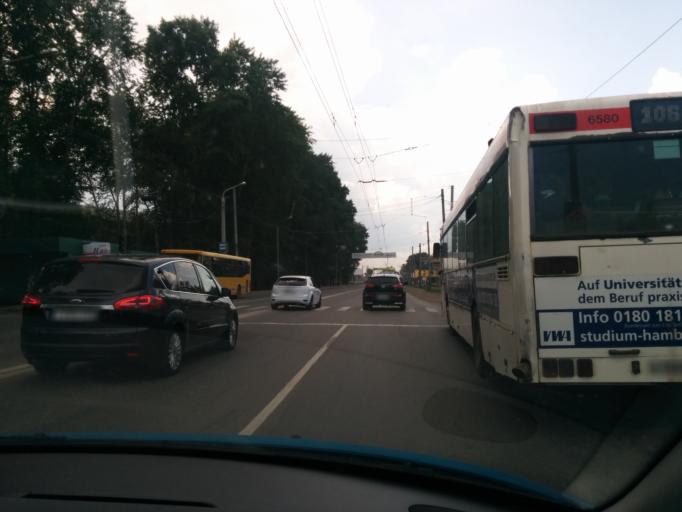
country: RU
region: Perm
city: Kondratovo
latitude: 57.9731
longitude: 56.1568
